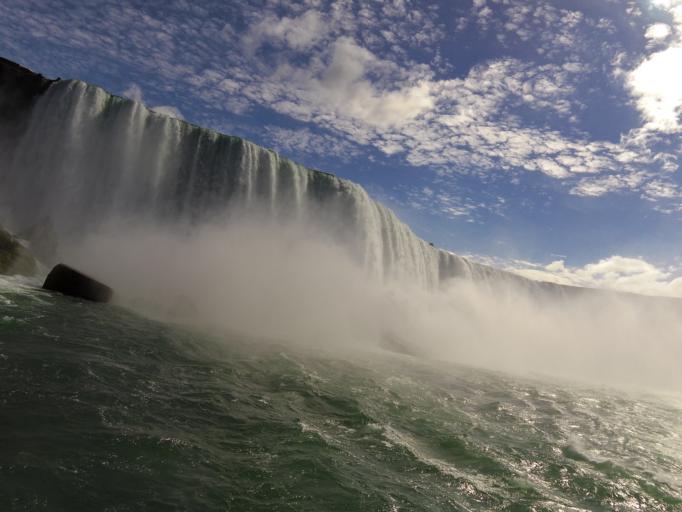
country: CA
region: Ontario
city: Niagara Falls
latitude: 43.0800
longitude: -79.0765
